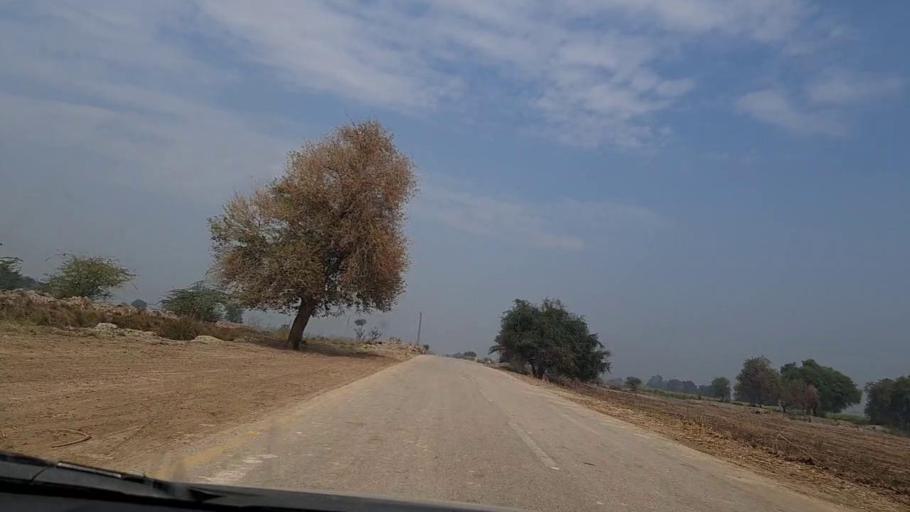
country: PK
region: Sindh
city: Daulatpur
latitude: 26.5248
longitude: 67.9733
